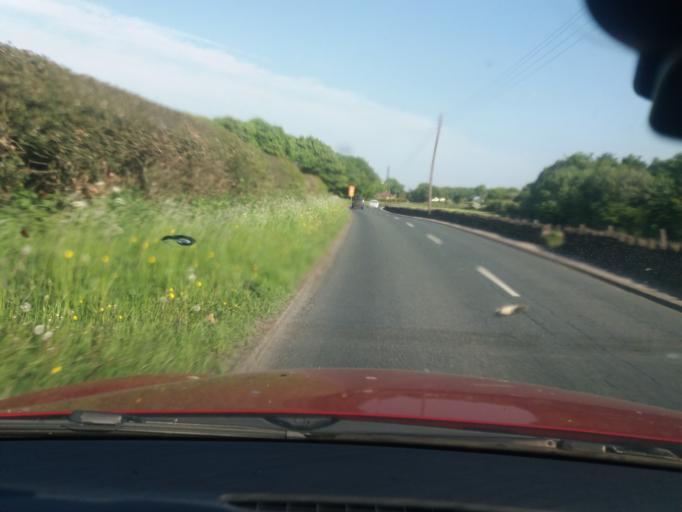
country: GB
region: England
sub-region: Lancashire
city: Adlington
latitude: 53.6329
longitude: -2.5946
